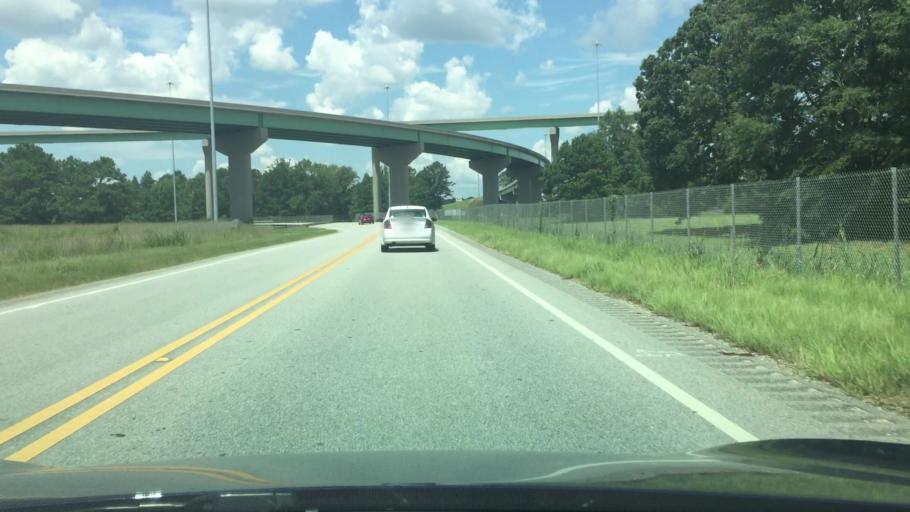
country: US
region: Alabama
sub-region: Montgomery County
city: Pike Road
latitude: 32.3668
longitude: -86.0776
